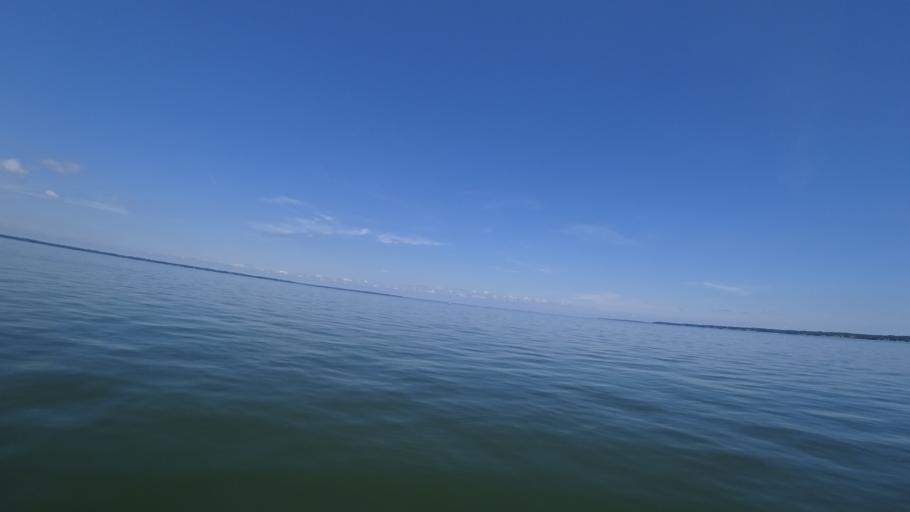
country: US
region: Virginia
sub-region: City of Newport News
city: Newport News
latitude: 37.0047
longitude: -76.4718
